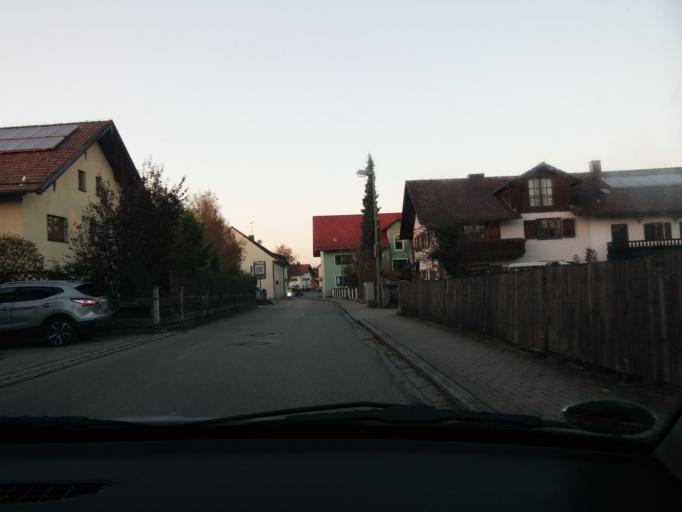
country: DE
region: Bavaria
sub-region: Upper Bavaria
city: Kirchseeon
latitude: 48.0806
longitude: 11.8600
